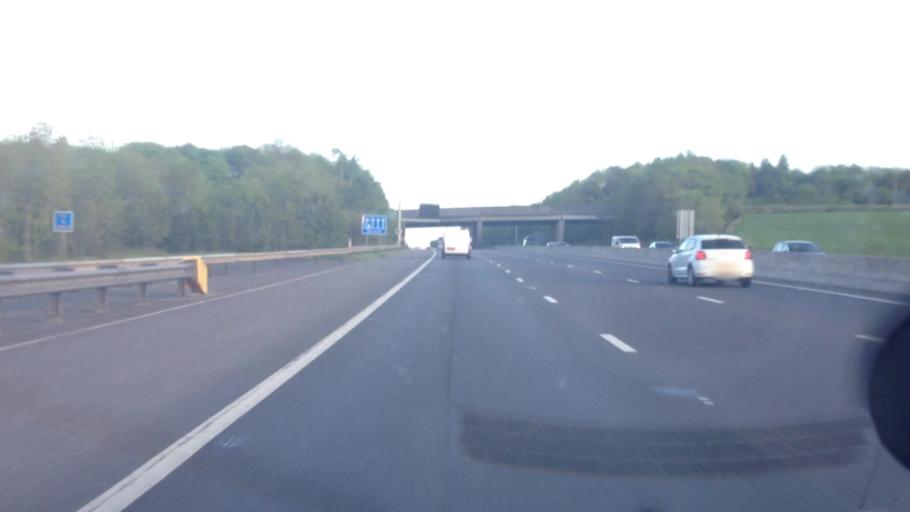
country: GB
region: England
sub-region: Sheffield
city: Chapletown
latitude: 53.4808
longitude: -1.4642
